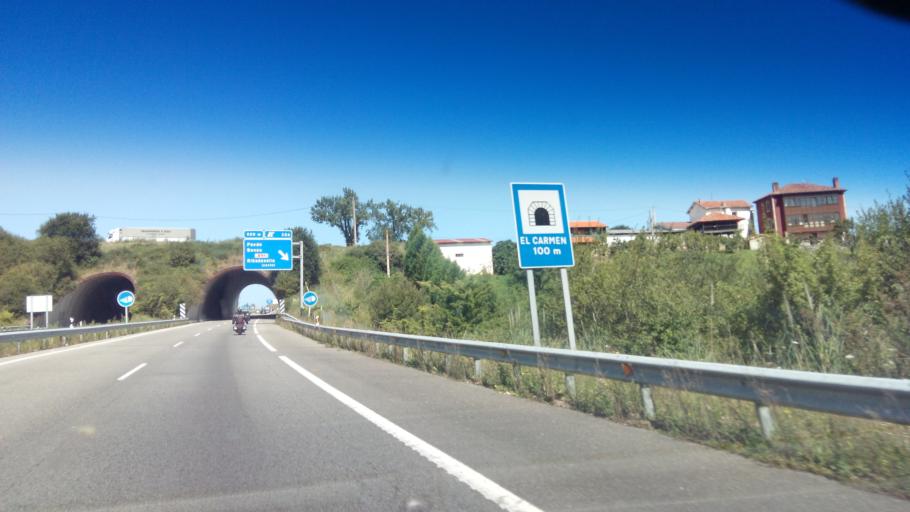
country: ES
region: Asturias
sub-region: Province of Asturias
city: Ribadesella
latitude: 43.4518
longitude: -5.1085
